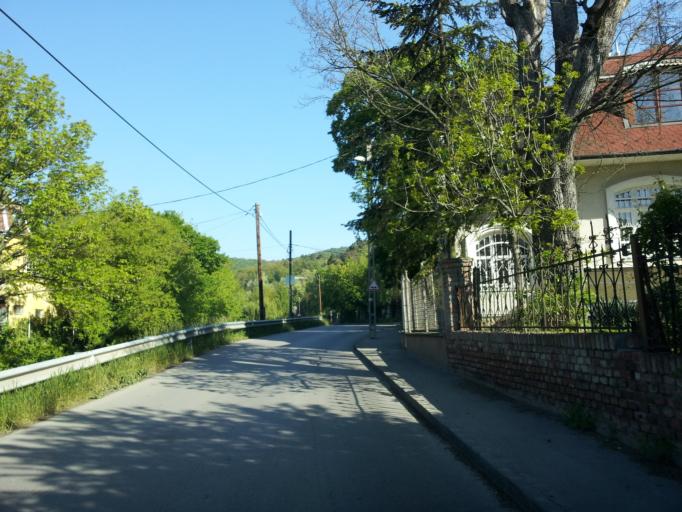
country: HU
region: Budapest
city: Budapest XII. keruelet
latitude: 47.5325
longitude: 18.9840
